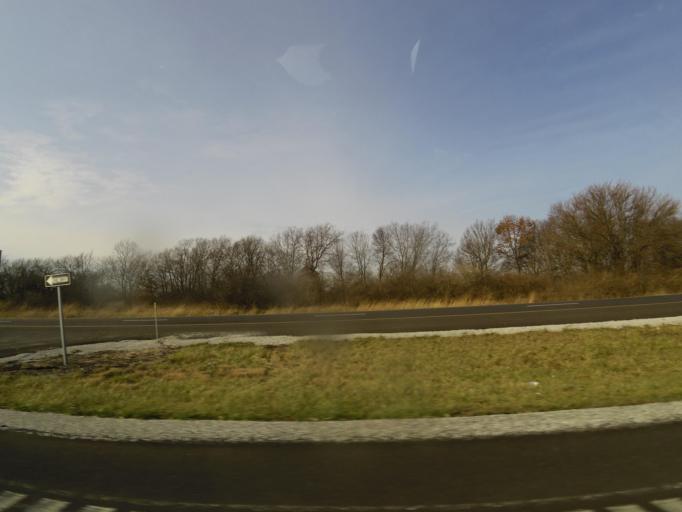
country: US
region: Illinois
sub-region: Macon County
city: Macon
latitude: 39.6835
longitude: -89.0051
